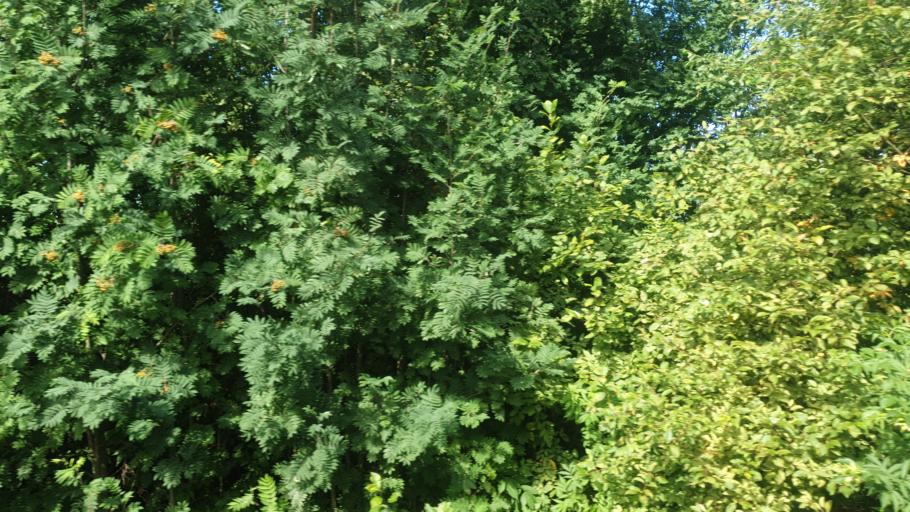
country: NO
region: Sor-Trondelag
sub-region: Orkdal
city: Orkanger
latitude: 63.2792
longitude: 9.8289
